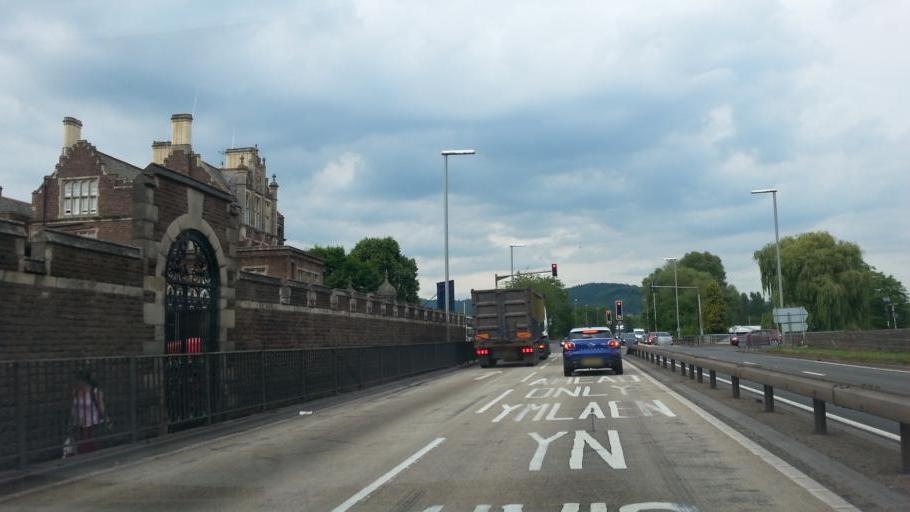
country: GB
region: Wales
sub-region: Monmouthshire
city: Monmouth
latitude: 51.8111
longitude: -2.7110
